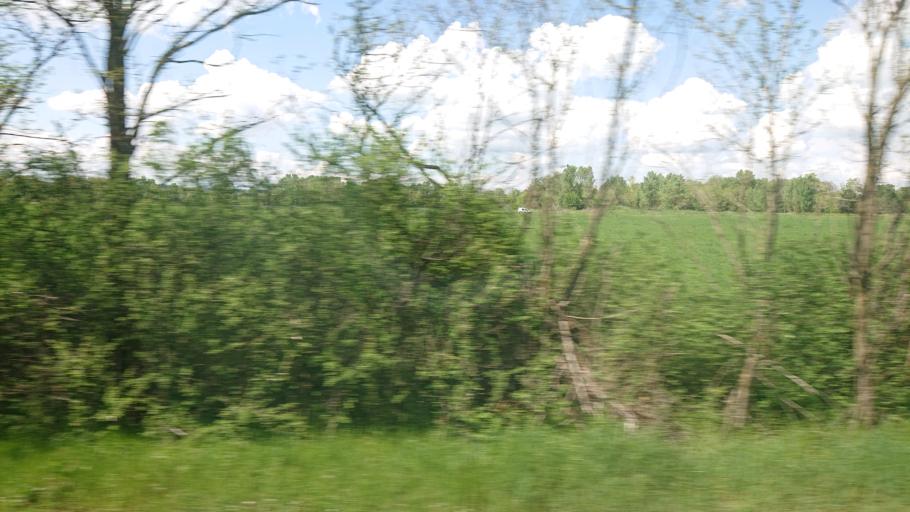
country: FR
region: Rhone-Alpes
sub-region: Departement de l'Ain
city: Saint-Denis-en-Bugey
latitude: 45.9470
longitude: 5.3123
